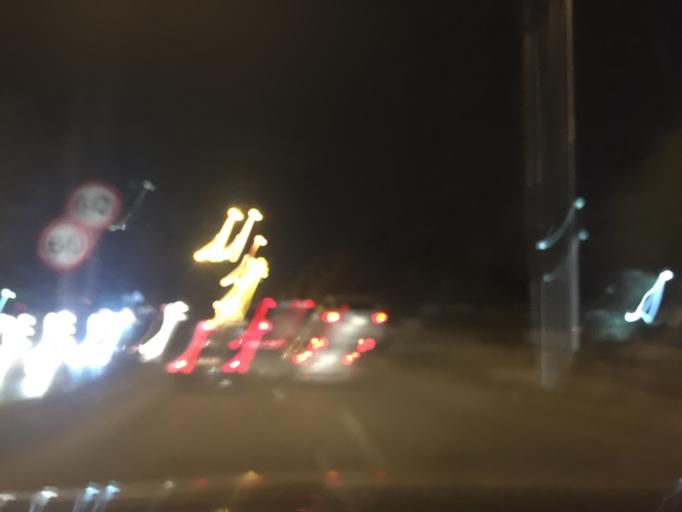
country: JO
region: Amman
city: Amman
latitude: 32.0033
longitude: 35.9339
